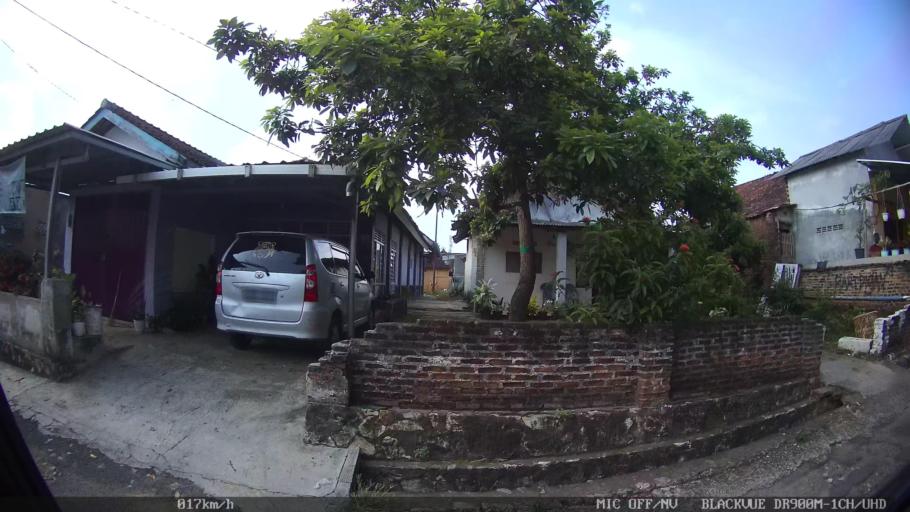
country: ID
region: Lampung
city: Kedaton
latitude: -5.3916
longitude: 105.2644
